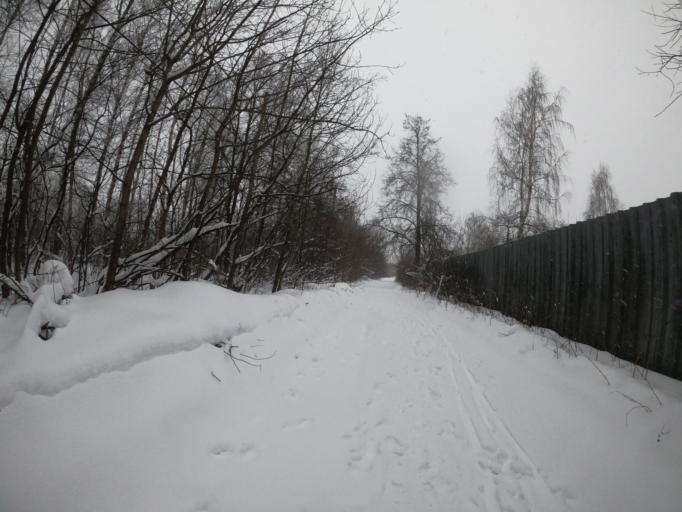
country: RU
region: Moskovskaya
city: Kupavna
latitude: 55.7479
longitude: 38.1423
